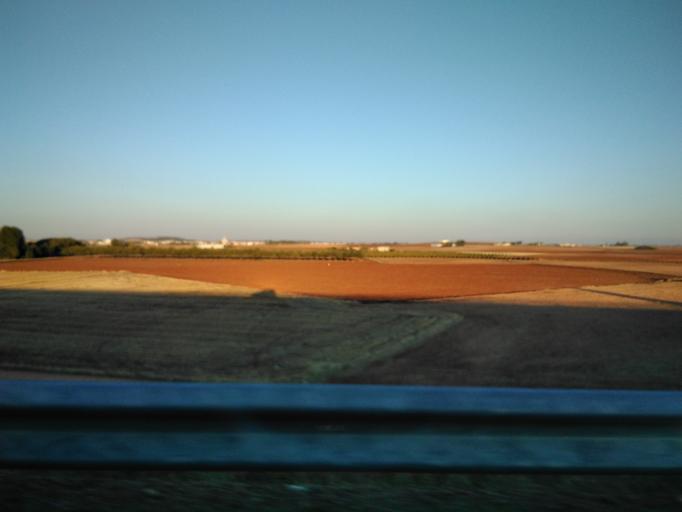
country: ES
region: Castille-La Mancha
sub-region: Provincia de Ciudad Real
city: Miguelturra
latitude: 38.9545
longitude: -3.9191
